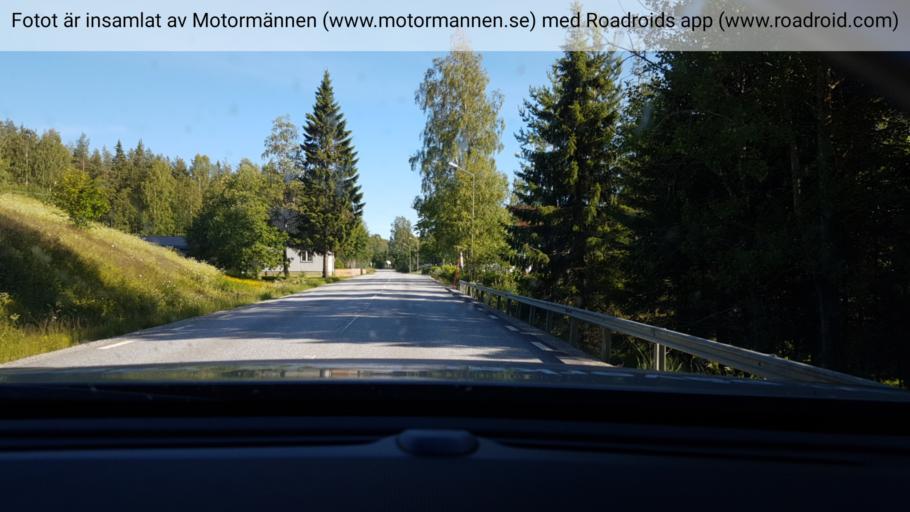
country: SE
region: Vaesterbotten
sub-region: Vindelns Kommun
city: Vindeln
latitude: 64.1553
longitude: 19.5079
